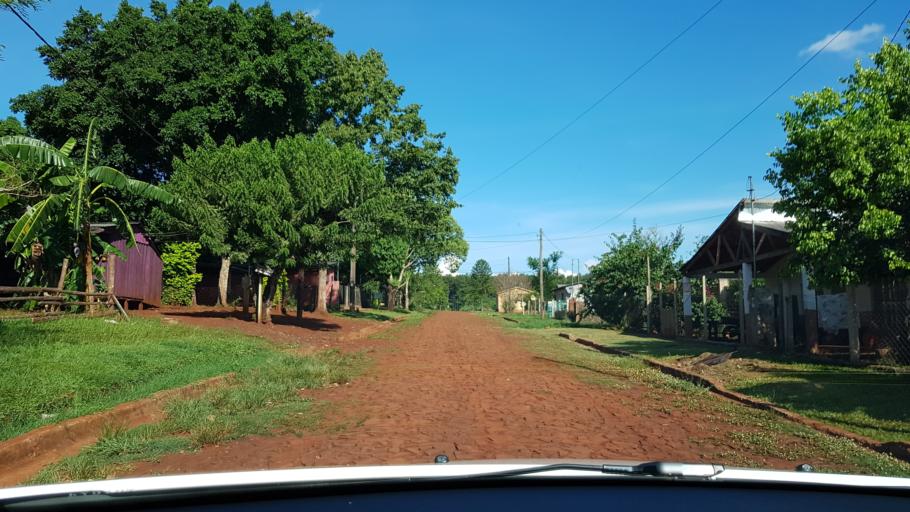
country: AR
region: Misiones
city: Puerto Libertad
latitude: -25.9132
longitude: -54.5827
